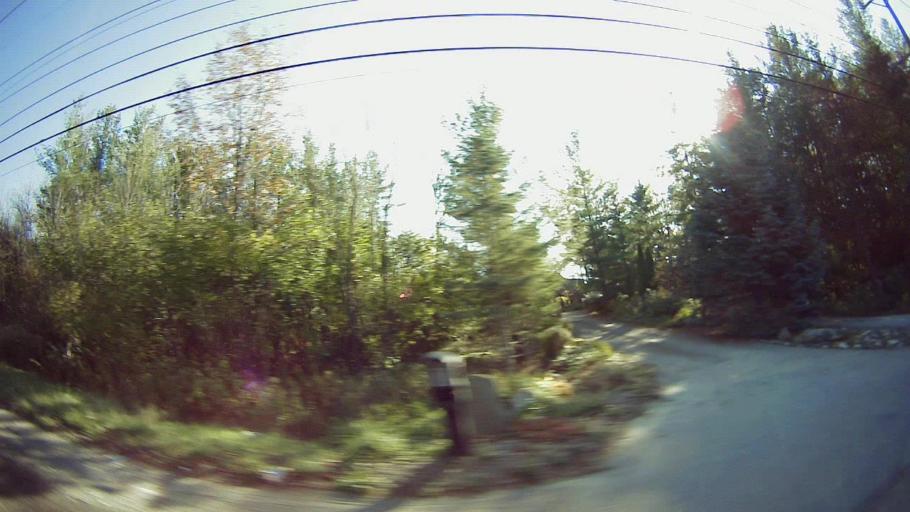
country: US
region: Michigan
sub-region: Oakland County
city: Franklin
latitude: 42.5436
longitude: -83.3343
